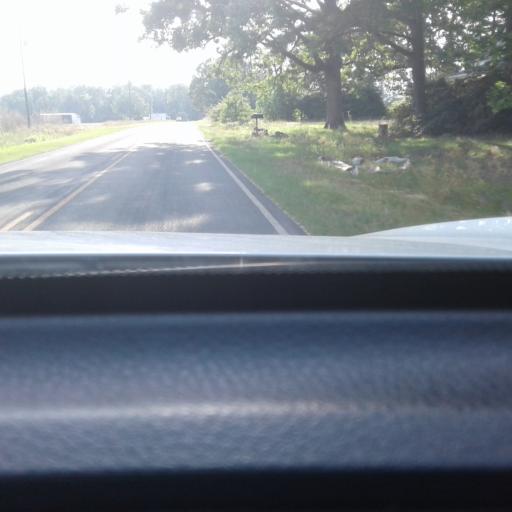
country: US
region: North Carolina
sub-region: Harnett County
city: Dunn
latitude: 35.3347
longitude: -78.5800
